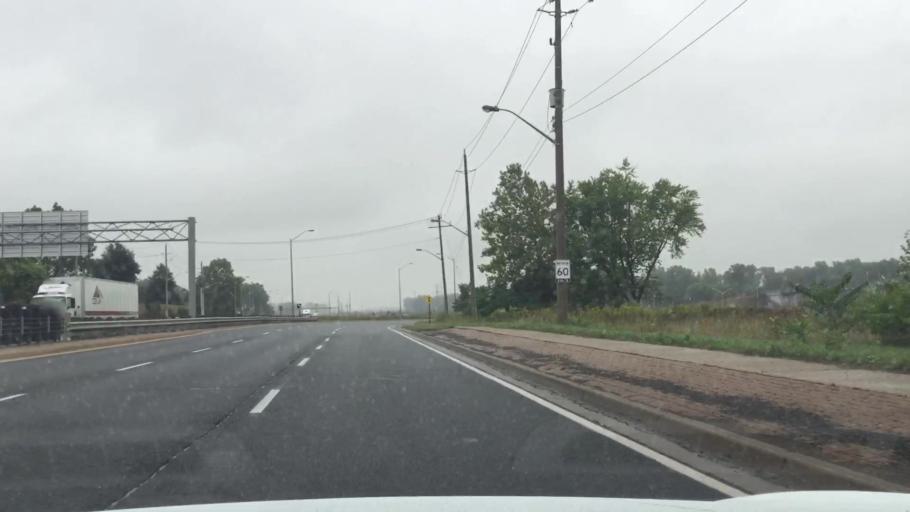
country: CA
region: Ontario
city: Windsor
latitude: 42.2692
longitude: -83.0468
